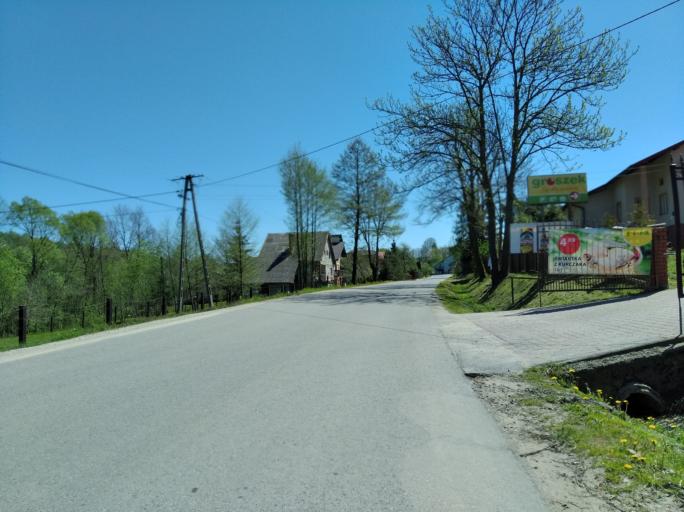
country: PL
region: Subcarpathian Voivodeship
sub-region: Powiat debicki
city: Brzostek
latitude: 49.9004
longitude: 21.4827
